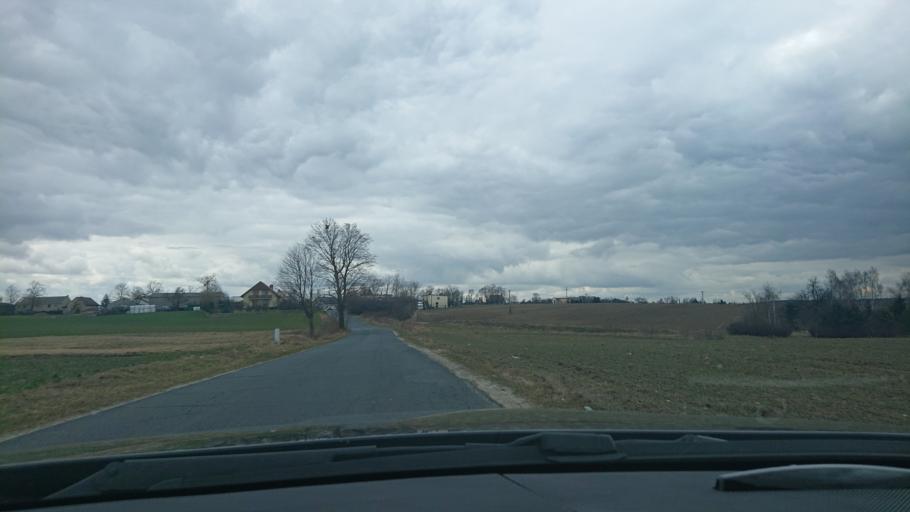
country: PL
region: Greater Poland Voivodeship
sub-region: Powiat gnieznienski
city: Gniezno
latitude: 52.5830
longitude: 17.6578
